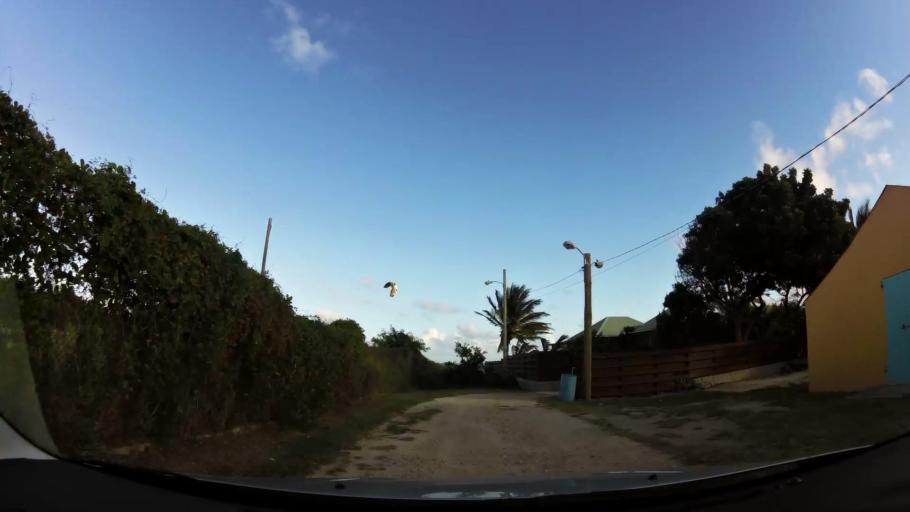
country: AG
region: Saint George
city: Piggotts
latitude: 17.1552
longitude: -61.7910
